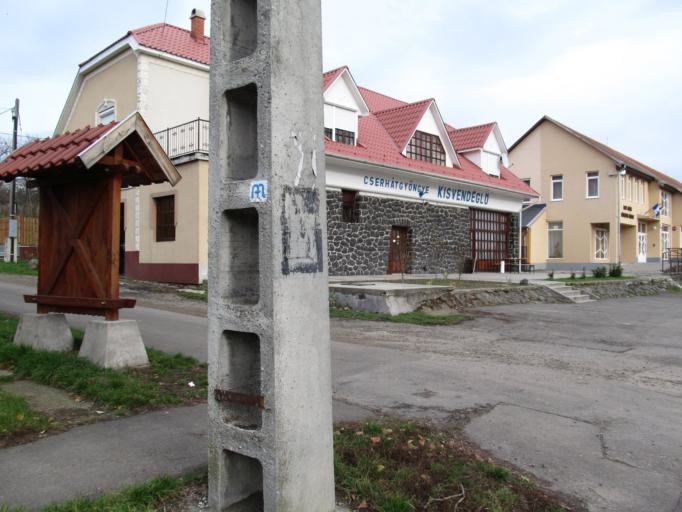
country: HU
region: Nograd
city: Bujak
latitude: 47.8836
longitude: 19.5484
